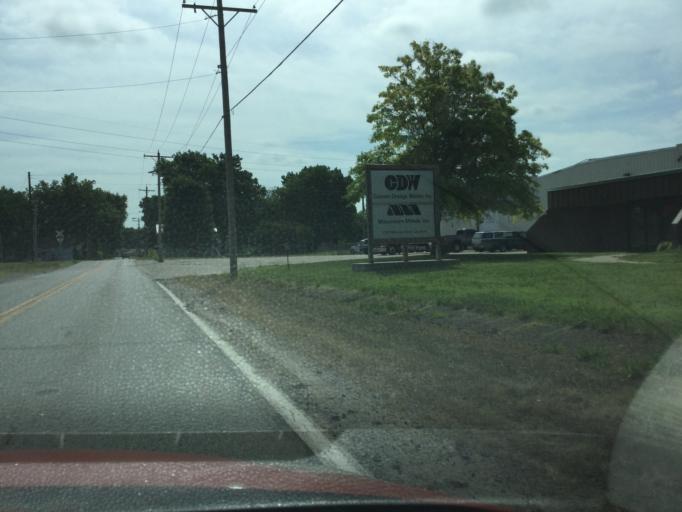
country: US
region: Kansas
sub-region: Shawnee County
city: Topeka
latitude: 39.0810
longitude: -95.6795
